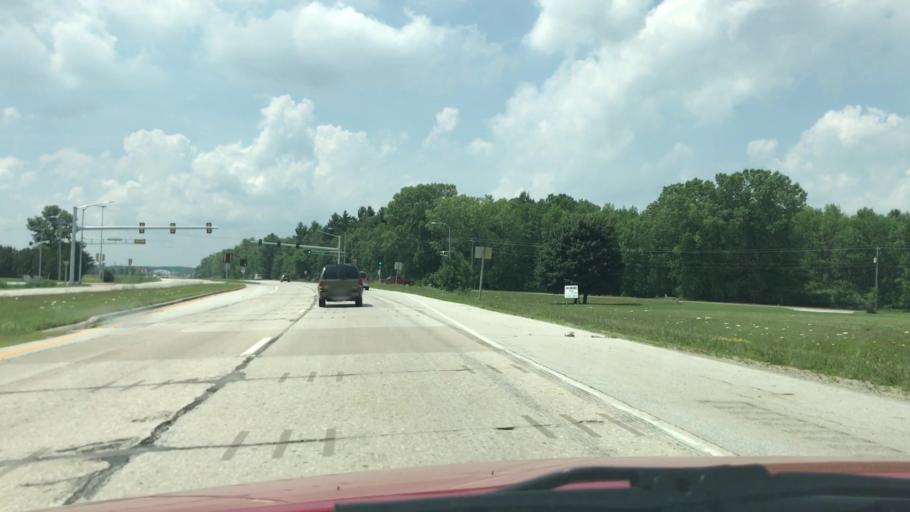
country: US
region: Wisconsin
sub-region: Brown County
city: Ashwaubenon
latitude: 44.4967
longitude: -88.1116
